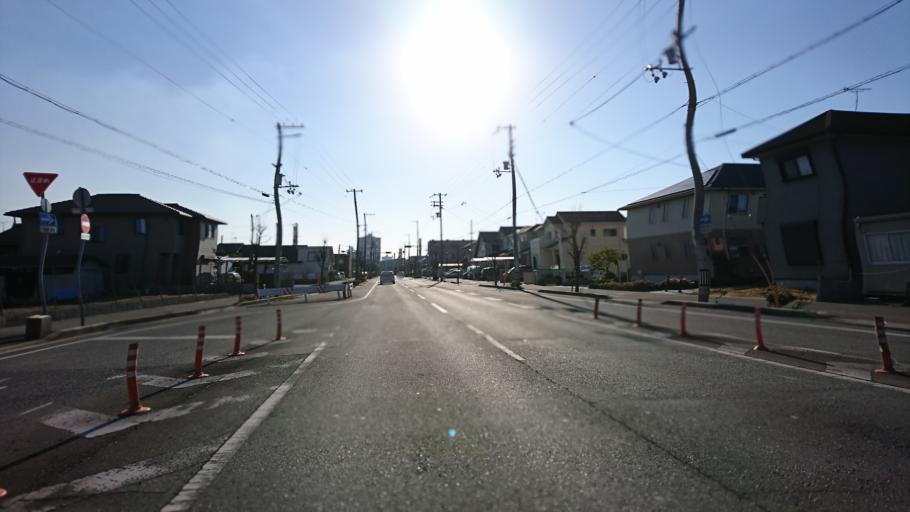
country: JP
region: Hyogo
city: Kakogawacho-honmachi
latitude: 34.7336
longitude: 134.8389
